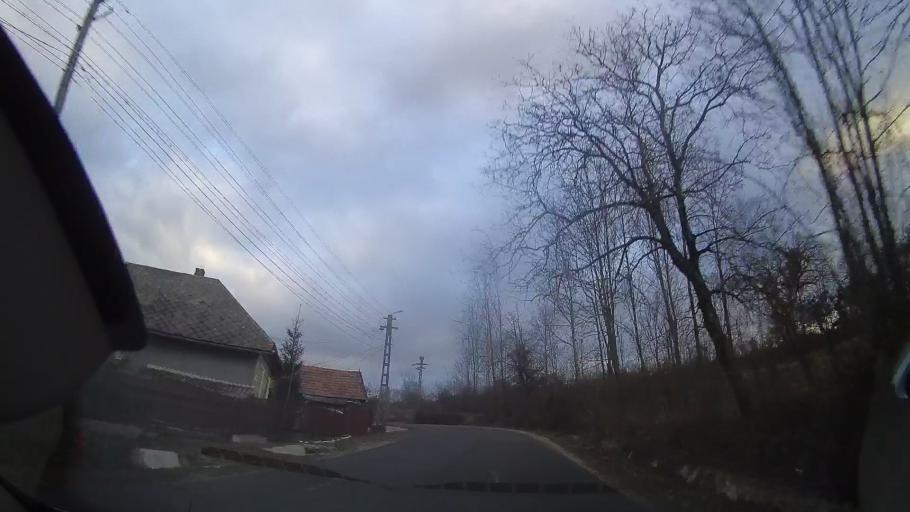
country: RO
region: Cluj
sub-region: Comuna Calatele
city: Calatele
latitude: 46.7824
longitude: 23.0223
